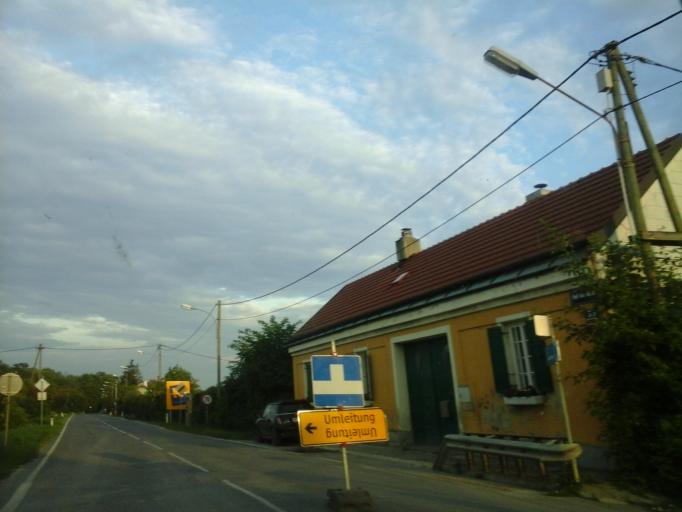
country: AT
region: Lower Austria
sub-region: Politischer Bezirk Wien-Umgebung
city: Schwechat
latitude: 48.1573
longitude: 16.4940
